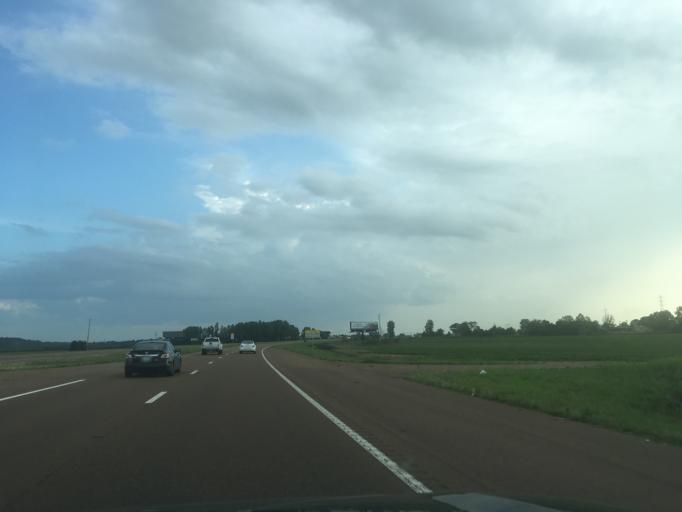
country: US
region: Mississippi
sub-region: De Soto County
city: Walls
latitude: 34.9535
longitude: -90.1433
